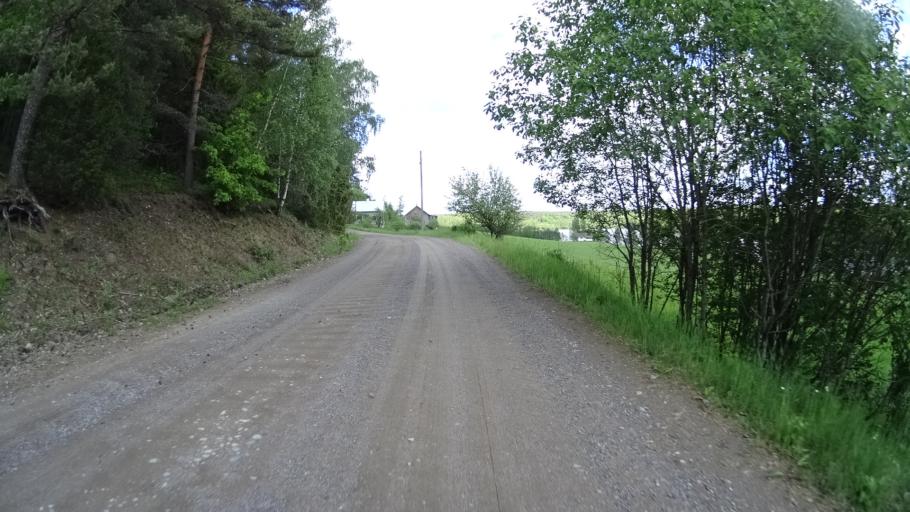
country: FI
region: Uusimaa
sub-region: Raaseporin
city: Pohja
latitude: 60.1212
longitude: 23.5952
